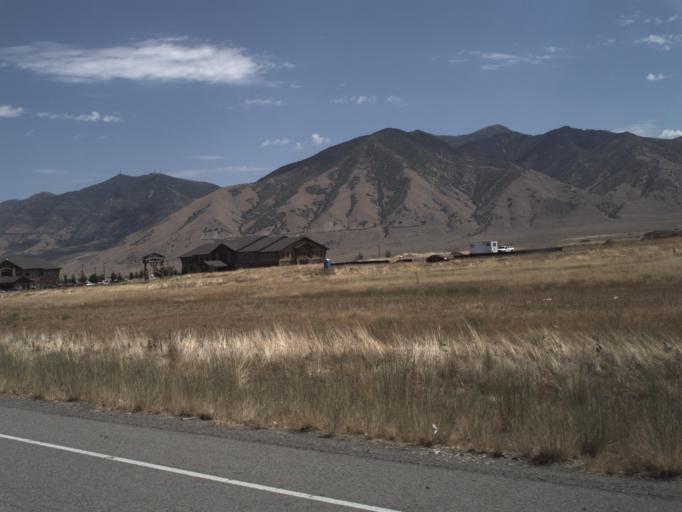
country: US
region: Utah
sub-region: Tooele County
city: Tooele
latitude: 40.5667
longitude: -112.2957
